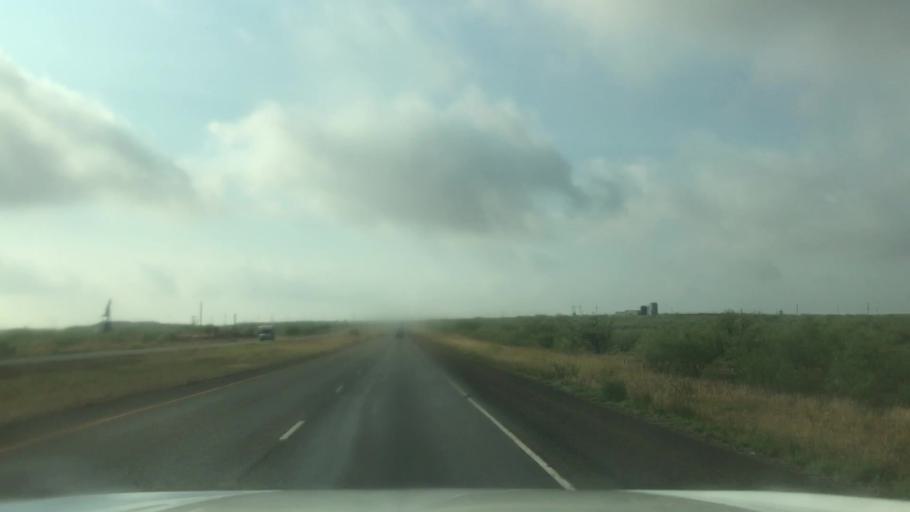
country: US
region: Texas
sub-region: Garza County
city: Post
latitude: 33.1687
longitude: -101.3538
